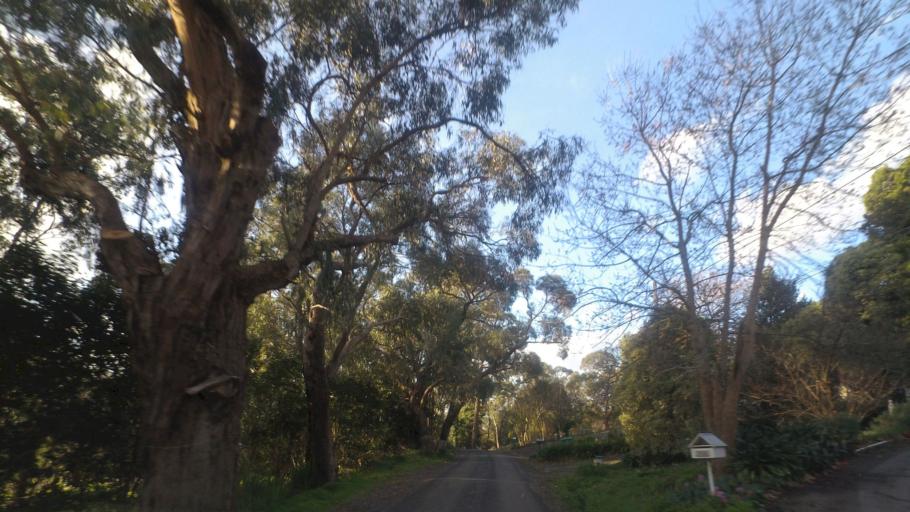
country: AU
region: Victoria
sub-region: Yarra Ranges
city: Kalorama
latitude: -37.8115
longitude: 145.3622
